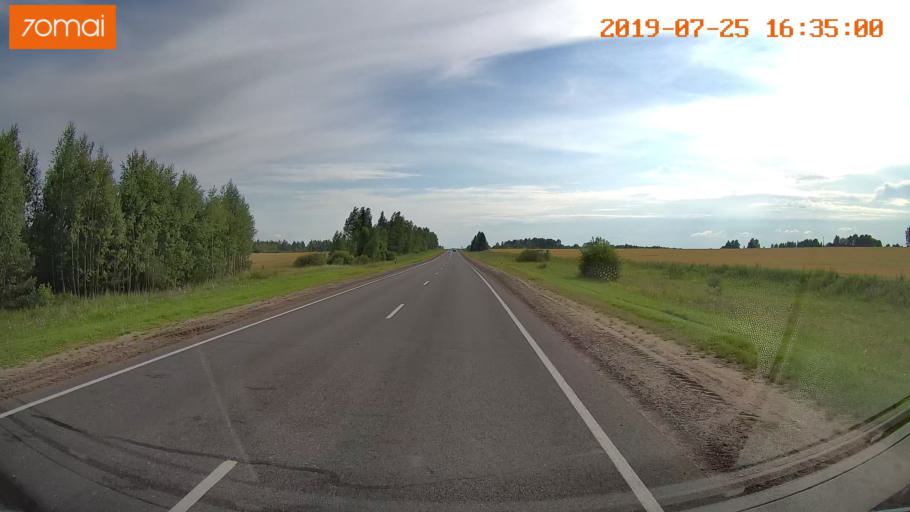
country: RU
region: Ivanovo
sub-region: Privolzhskiy Rayon
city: Ples
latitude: 57.4109
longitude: 41.4271
